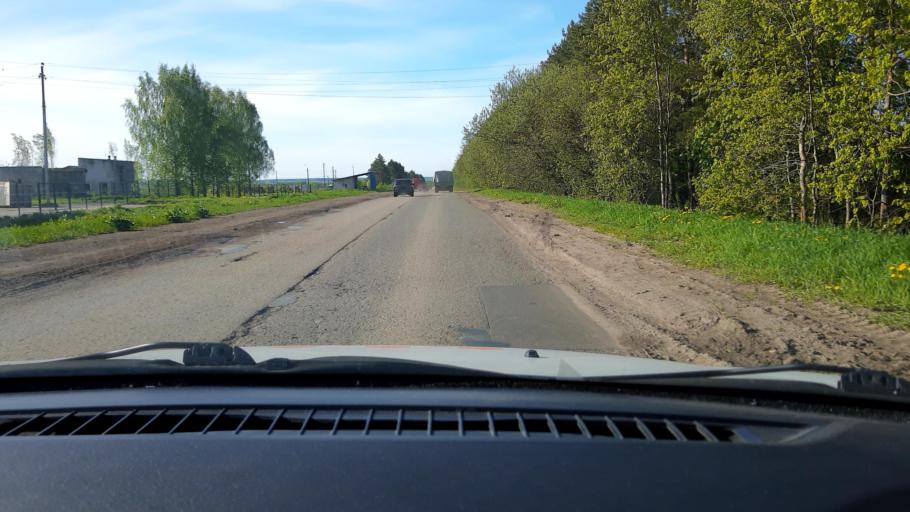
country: RU
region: Nizjnij Novgorod
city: Burevestnik
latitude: 56.1552
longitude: 43.7770
